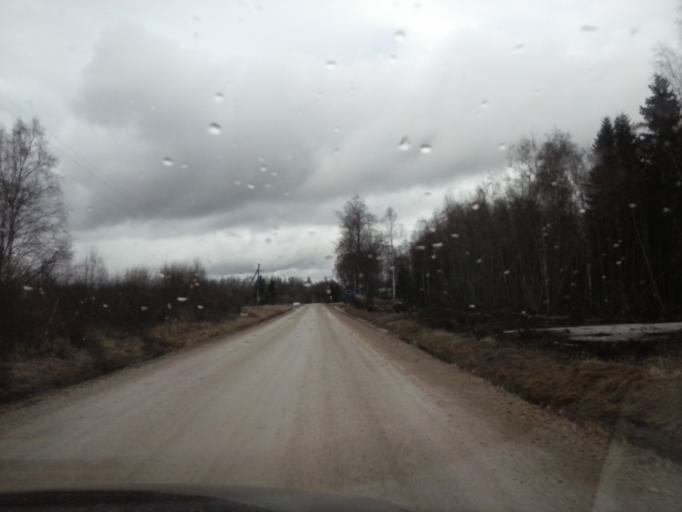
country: EE
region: Ida-Virumaa
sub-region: Kivioli linn
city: Kivioli
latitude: 59.1101
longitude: 26.9232
